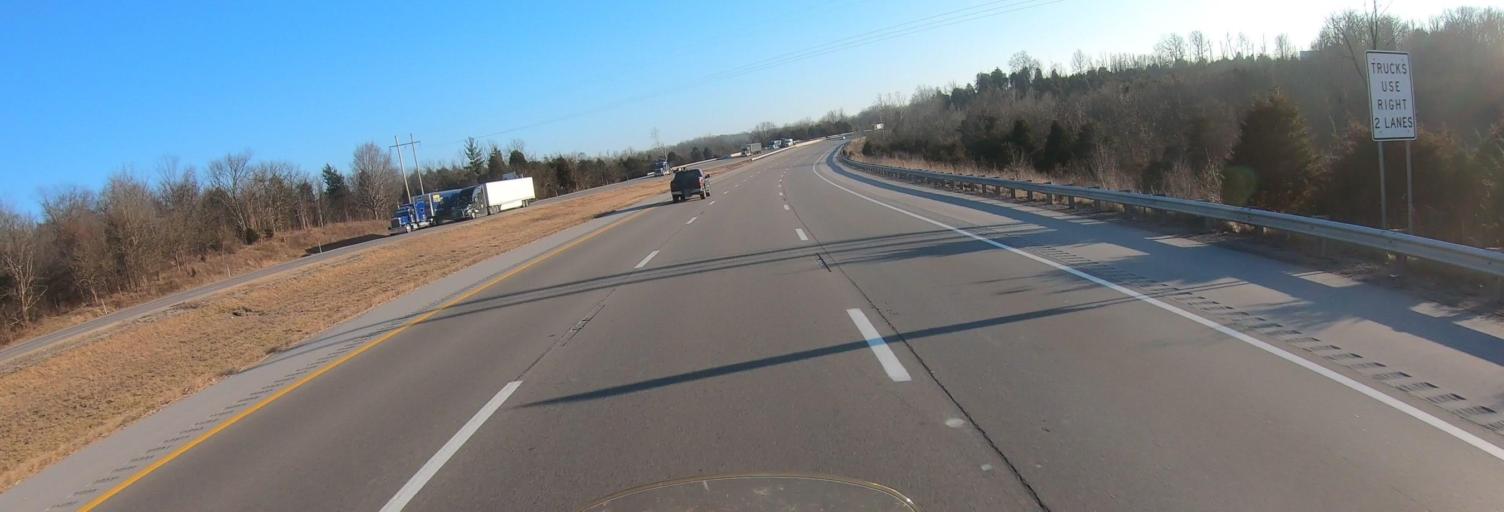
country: US
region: Kentucky
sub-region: Scott County
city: Georgetown
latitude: 38.3634
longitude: -84.5687
